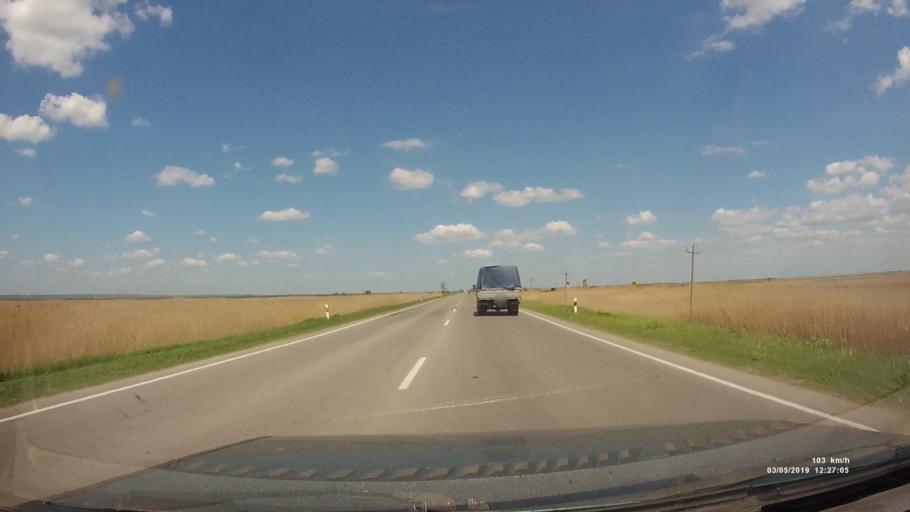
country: RU
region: Rostov
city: Semikarakorsk
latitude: 47.4547
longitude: 40.7185
